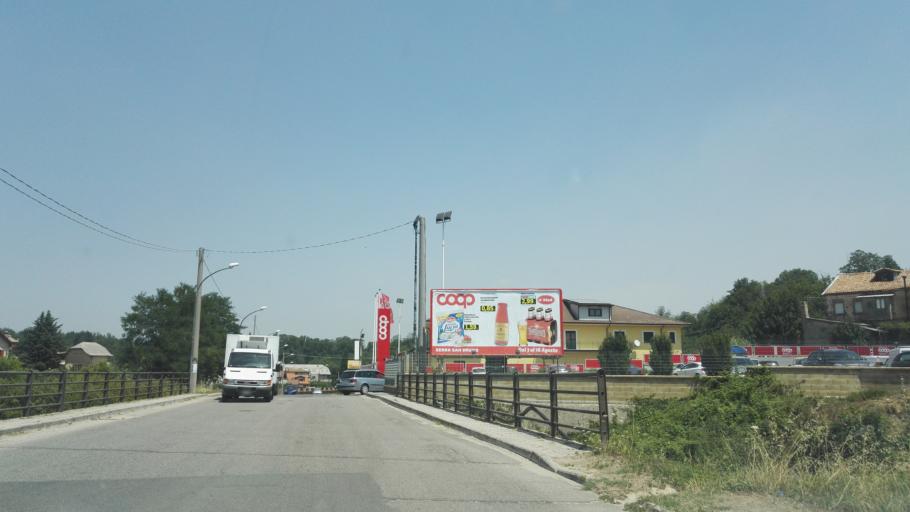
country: IT
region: Calabria
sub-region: Provincia di Vibo-Valentia
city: Serra San Bruno
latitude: 38.5764
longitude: 16.3323
